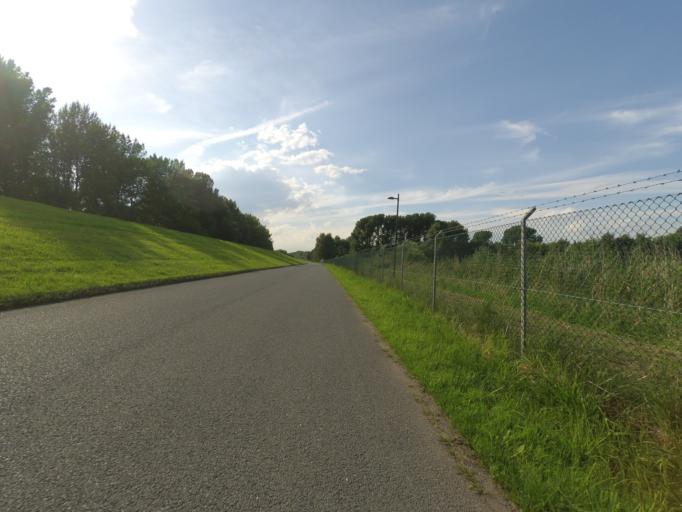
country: DE
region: Hamburg
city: Rothenburgsort
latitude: 53.5253
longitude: 10.0501
